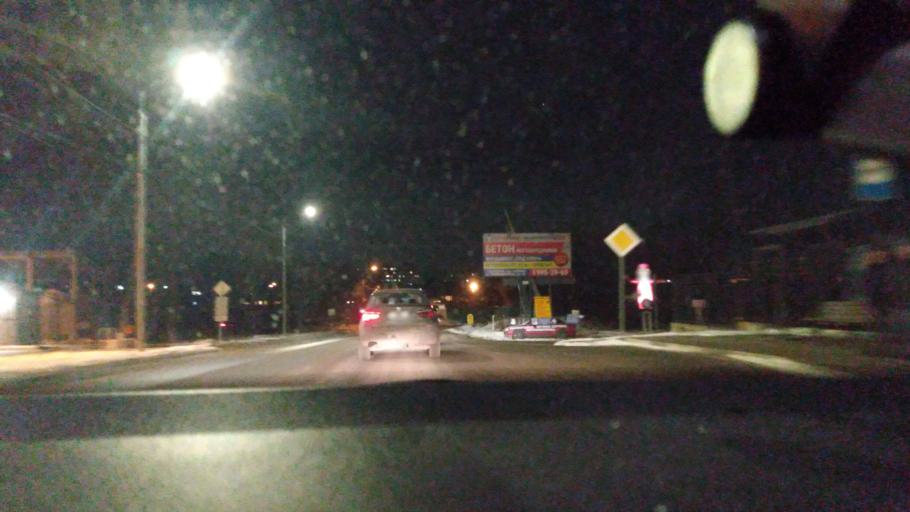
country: RU
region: Moskovskaya
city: Zheleznodorozhnyy
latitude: 55.7273
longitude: 38.0324
